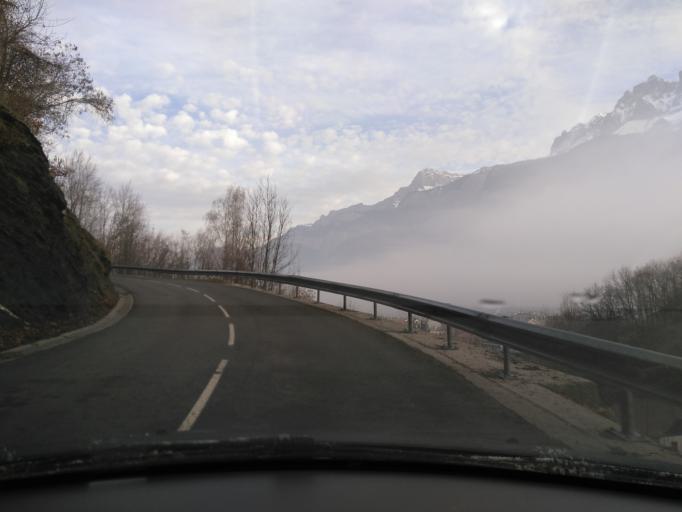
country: FR
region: Rhone-Alpes
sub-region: Departement de la Haute-Savoie
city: Sallanches
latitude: 45.9337
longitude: 6.6274
